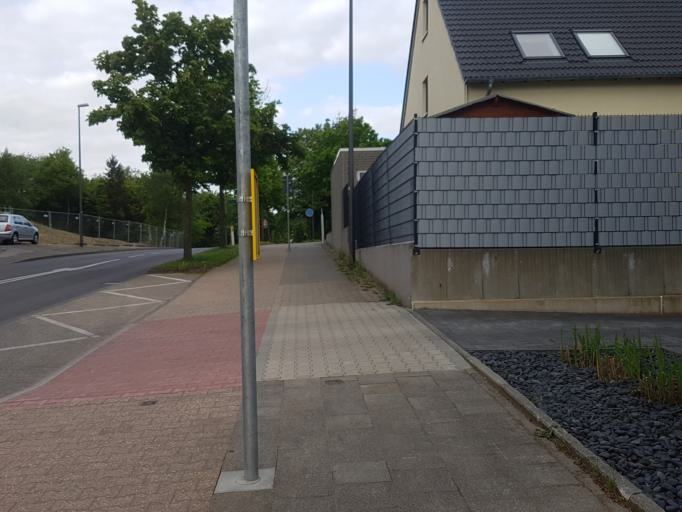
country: DE
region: North Rhine-Westphalia
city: Stolberg
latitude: 50.7816
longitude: 6.1739
